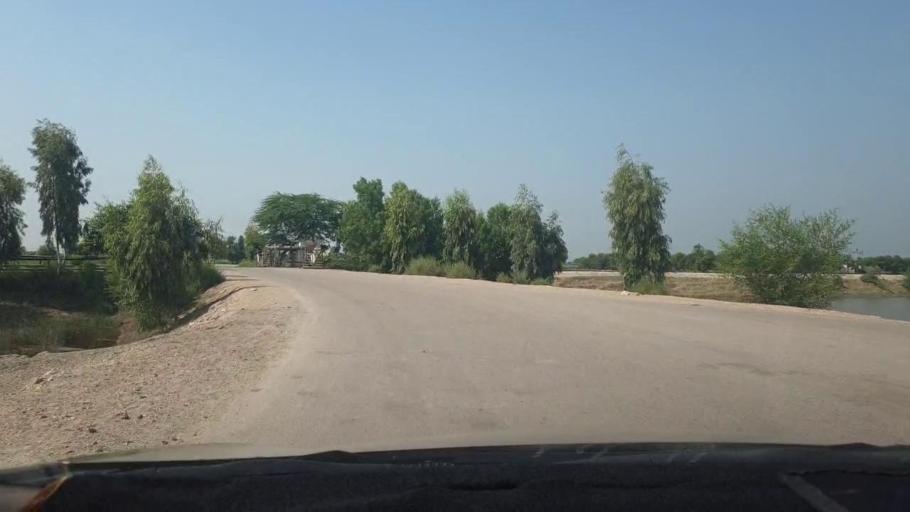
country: PK
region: Sindh
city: Larkana
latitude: 27.5977
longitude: 68.2436
